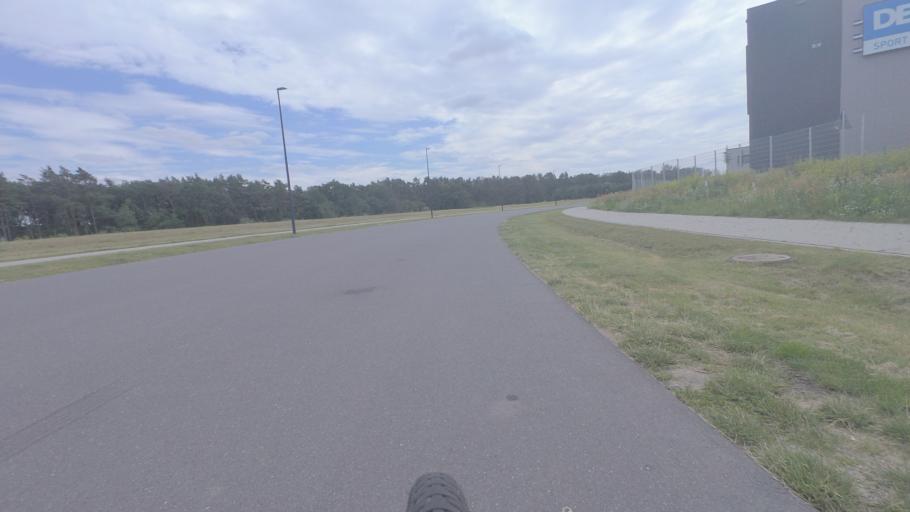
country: DE
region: Brandenburg
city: Grossbeeren
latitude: 52.3188
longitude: 13.3026
